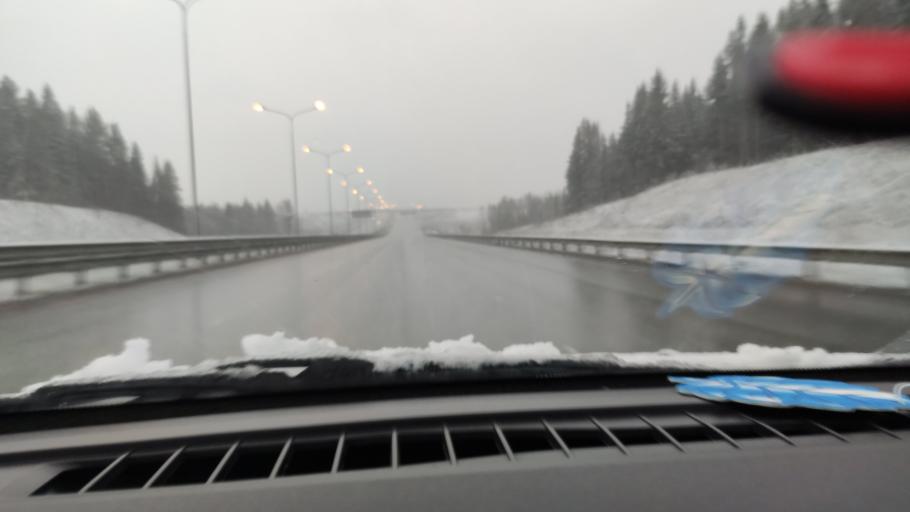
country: RU
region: Perm
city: Lobanovo
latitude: 57.8159
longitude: 56.3113
